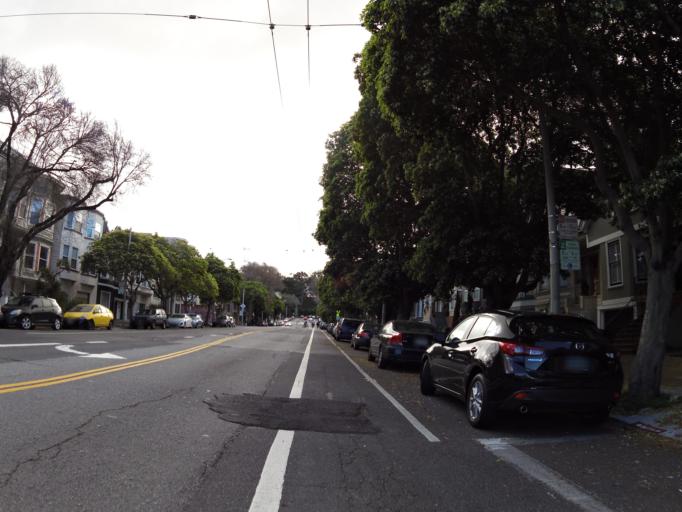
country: US
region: California
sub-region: San Francisco County
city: San Francisco
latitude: 37.7770
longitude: -122.4586
